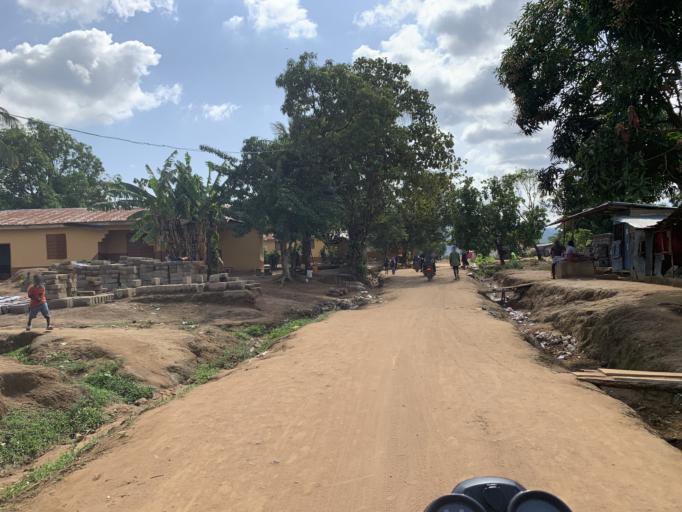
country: SL
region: Western Area
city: Waterloo
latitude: 8.3312
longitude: -13.0551
